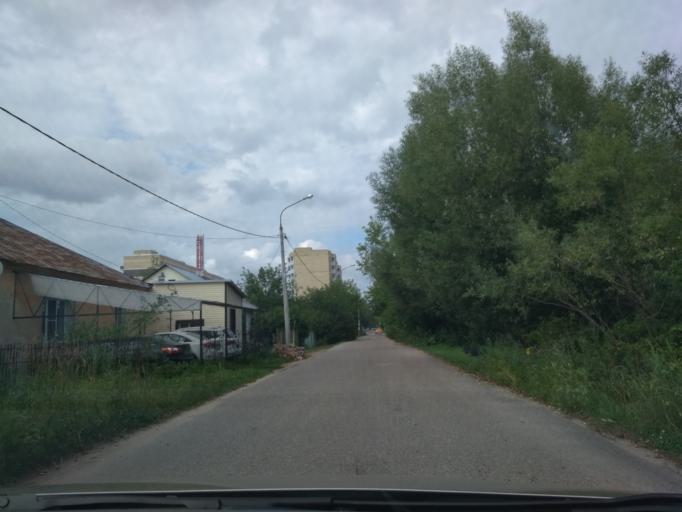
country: RU
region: Moskovskaya
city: Kabanovo
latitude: 55.7852
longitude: 38.9264
